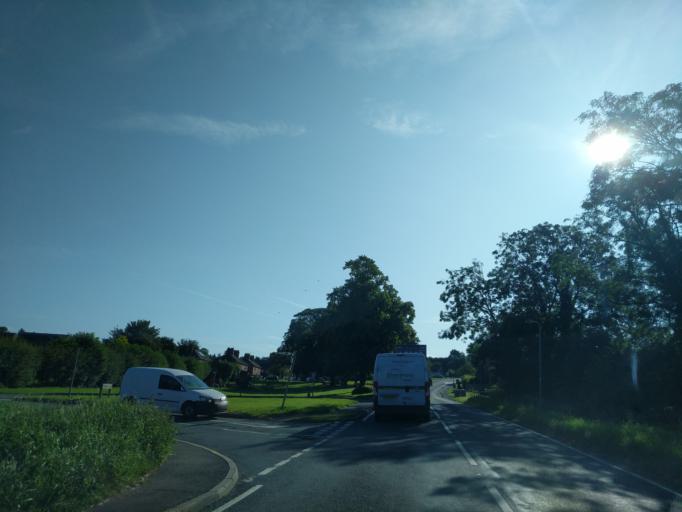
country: GB
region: England
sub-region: District of Rutland
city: Clipsham
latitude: 52.8122
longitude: -0.5239
